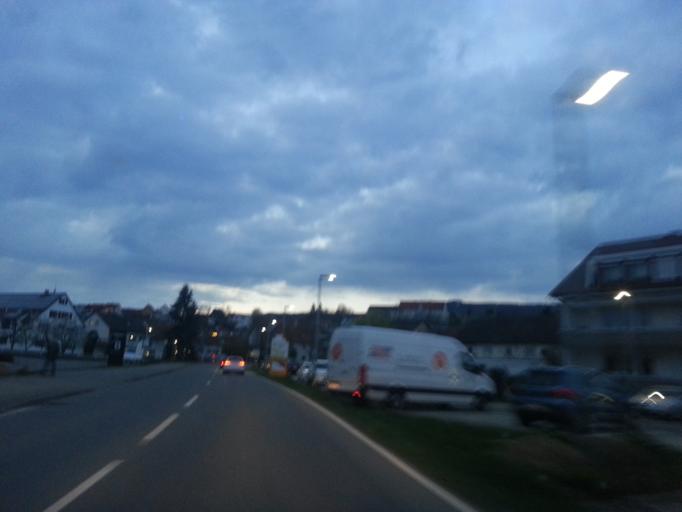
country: DE
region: Baden-Wuerttemberg
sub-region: Tuebingen Region
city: Markdorf
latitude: 47.7169
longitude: 9.3961
